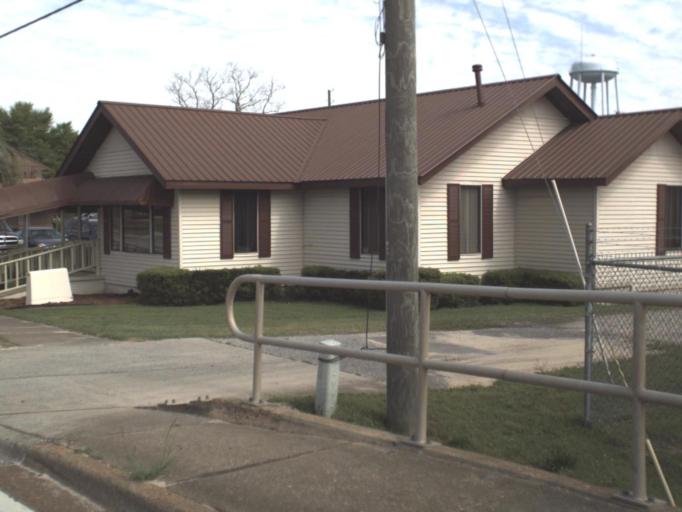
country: US
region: Florida
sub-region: Okaloosa County
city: Crestview
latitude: 30.7596
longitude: -86.5693
